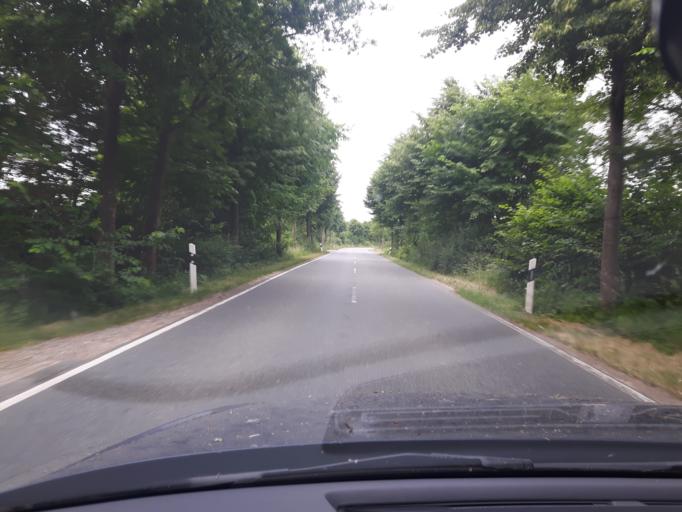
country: DE
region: Schleswig-Holstein
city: Ratekau
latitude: 53.9507
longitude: 10.7552
